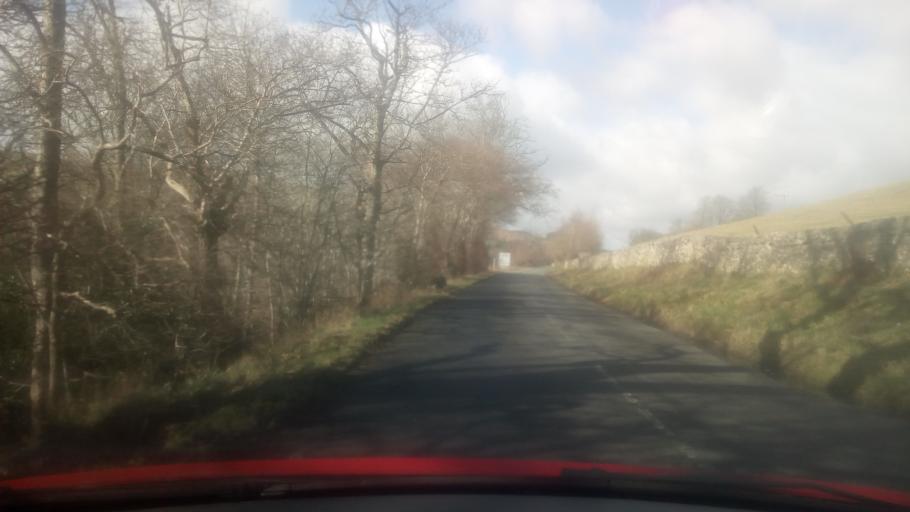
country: GB
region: Scotland
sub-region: The Scottish Borders
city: Selkirk
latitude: 55.6065
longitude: -2.8924
